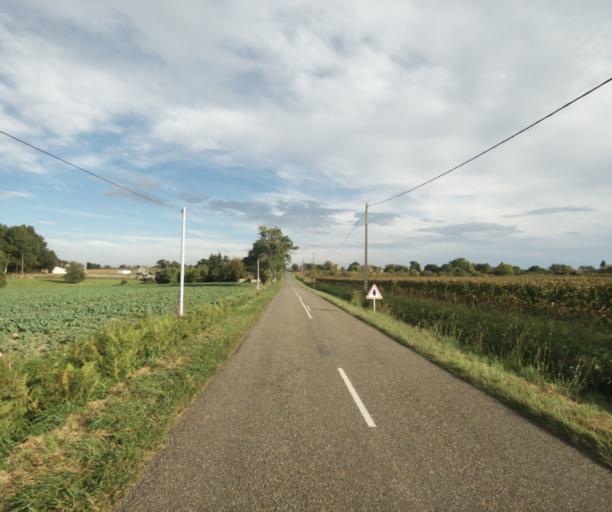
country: FR
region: Midi-Pyrenees
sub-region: Departement du Gers
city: Le Houga
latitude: 43.8578
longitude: -0.1453
